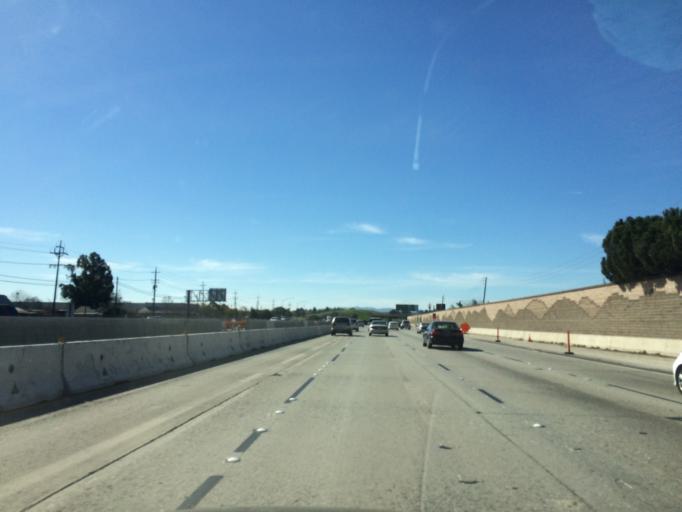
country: US
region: California
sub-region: Alameda County
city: Livermore
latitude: 37.7054
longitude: -121.7327
